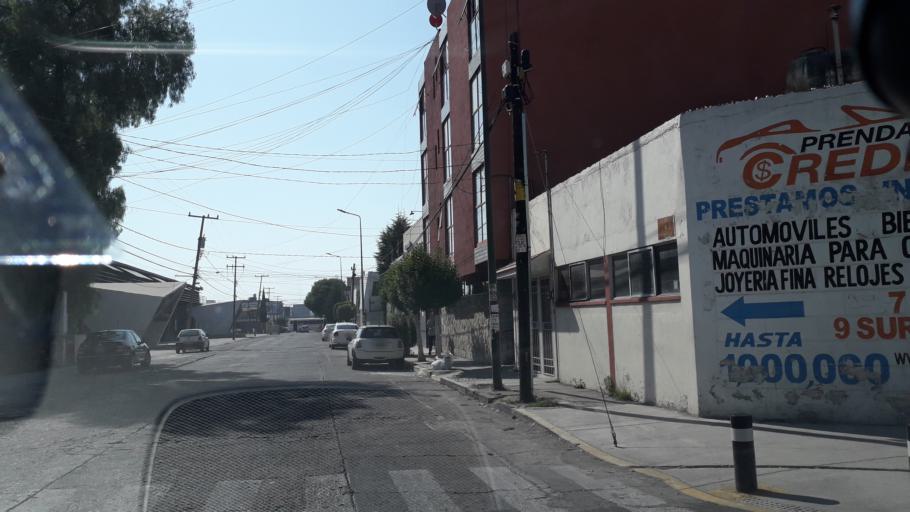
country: MX
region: Puebla
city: Puebla
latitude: 19.0319
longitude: -98.2138
